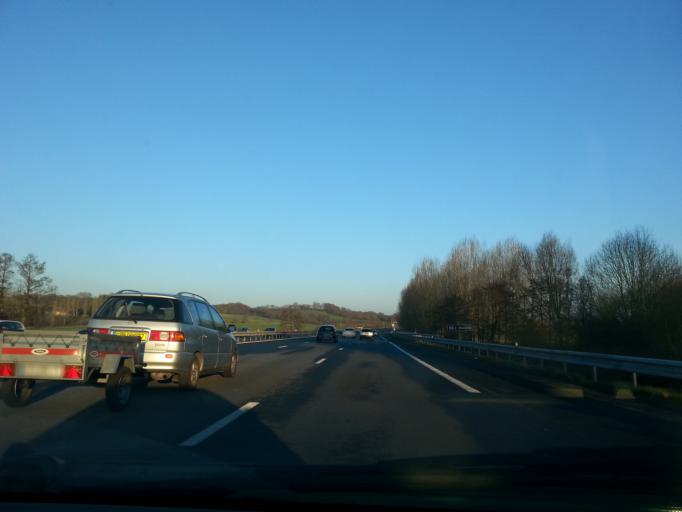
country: FR
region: Pays de la Loire
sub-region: Departement de la Sarthe
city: Le Luart
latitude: 48.1153
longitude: 0.5801
